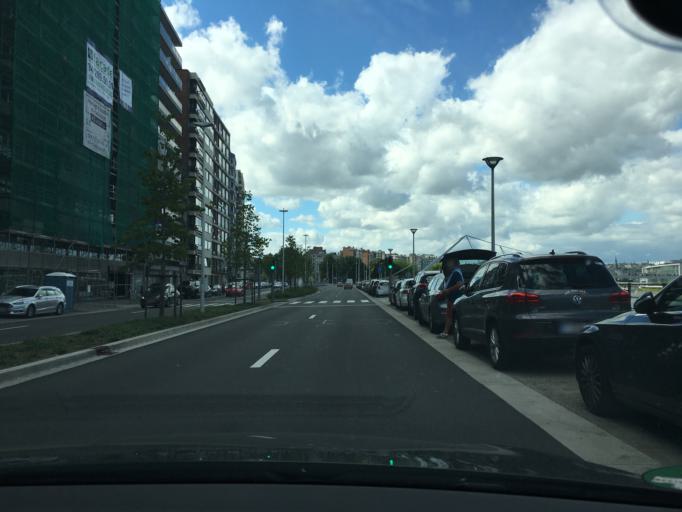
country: BE
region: Wallonia
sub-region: Province de Liege
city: Liege
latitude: 50.6257
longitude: 5.5750
